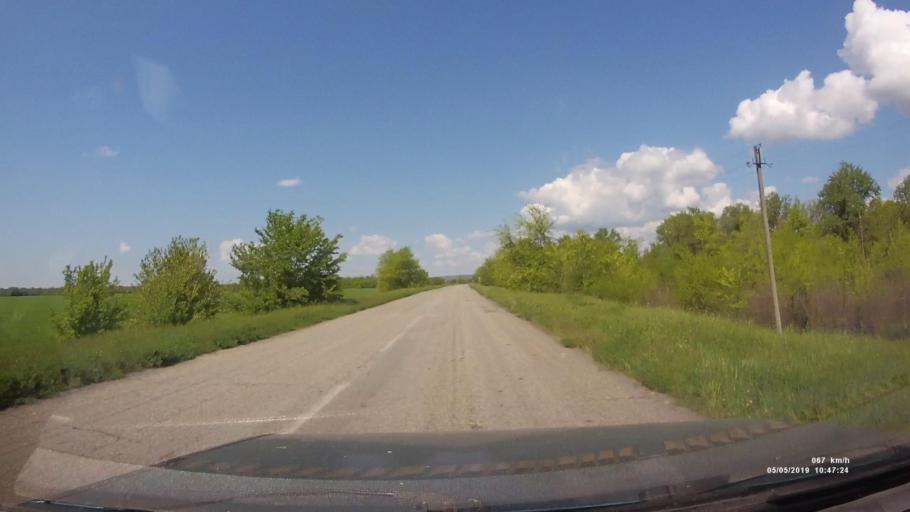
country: RU
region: Rostov
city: Ust'-Donetskiy
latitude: 47.6383
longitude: 40.8333
